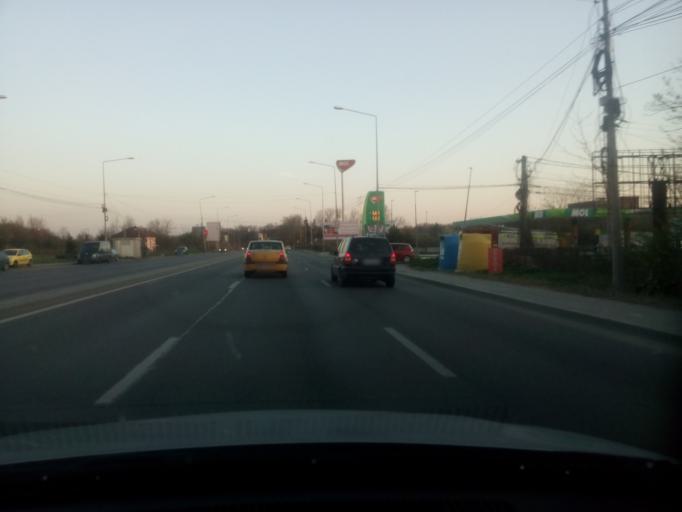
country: RO
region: Ilfov
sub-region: Comuna Otopeni
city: Otopeni
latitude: 44.5287
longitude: 26.0703
